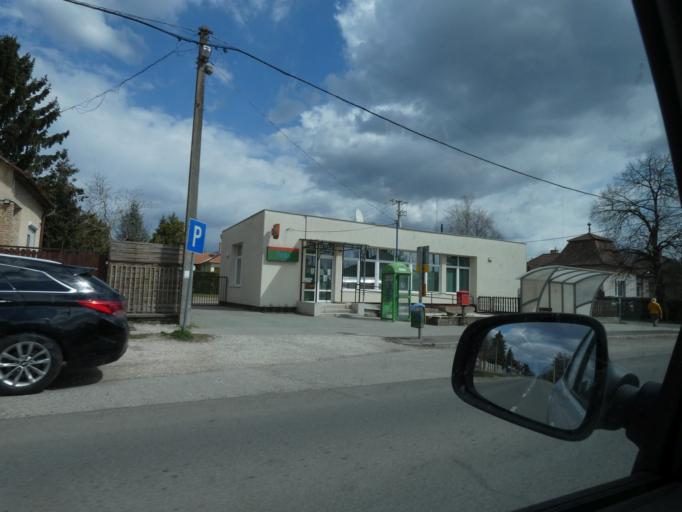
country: HU
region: Pest
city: Isaszeg
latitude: 47.5350
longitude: 19.3977
